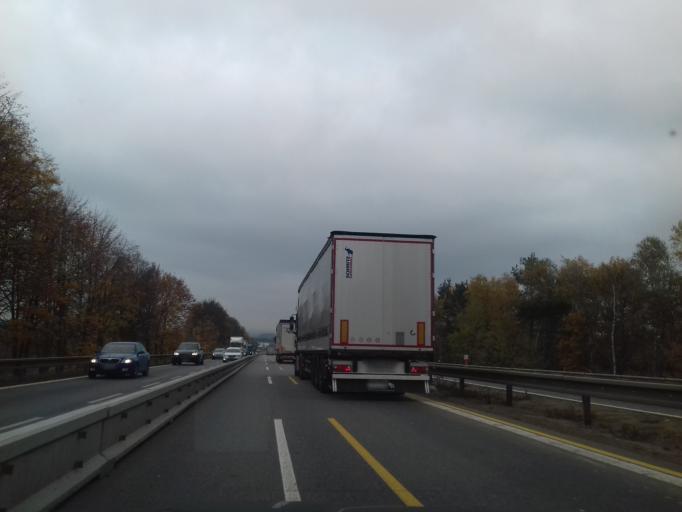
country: CZ
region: Central Bohemia
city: Trhovy Stepanov
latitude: 49.7305
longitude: 15.0447
